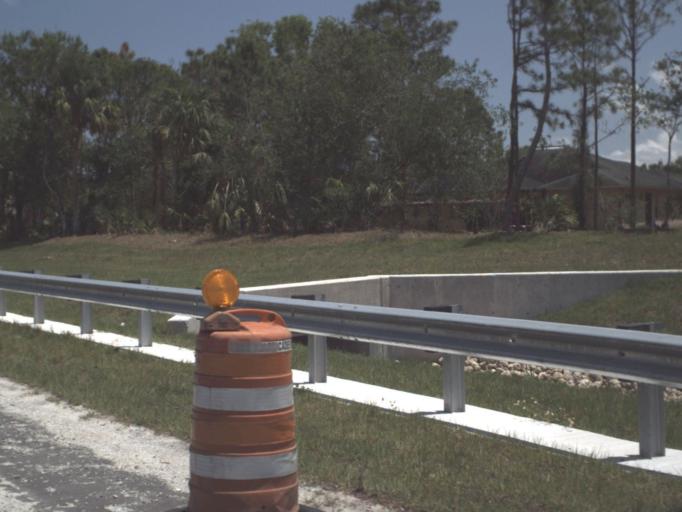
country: US
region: Florida
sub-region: Saint Lucie County
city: White City
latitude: 27.3744
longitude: -80.3701
